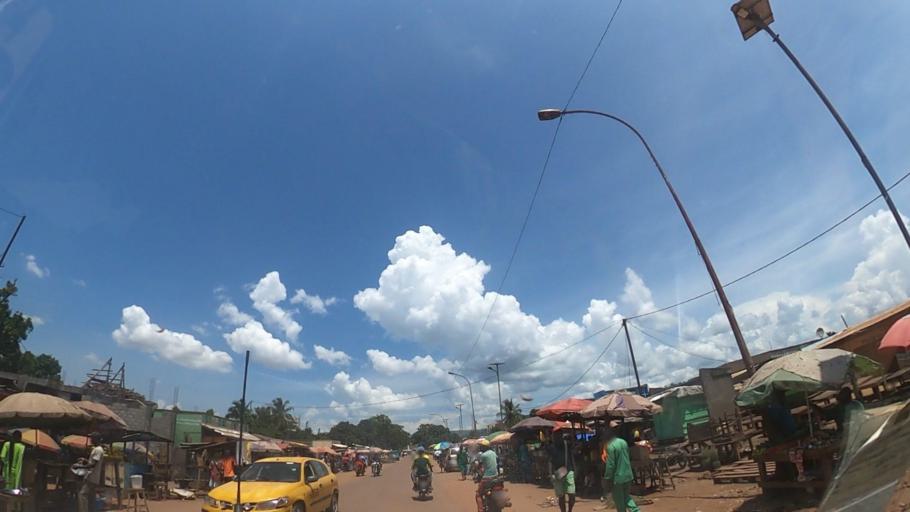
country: CF
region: Bangui
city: Bangui
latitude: 4.3631
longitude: 18.5611
